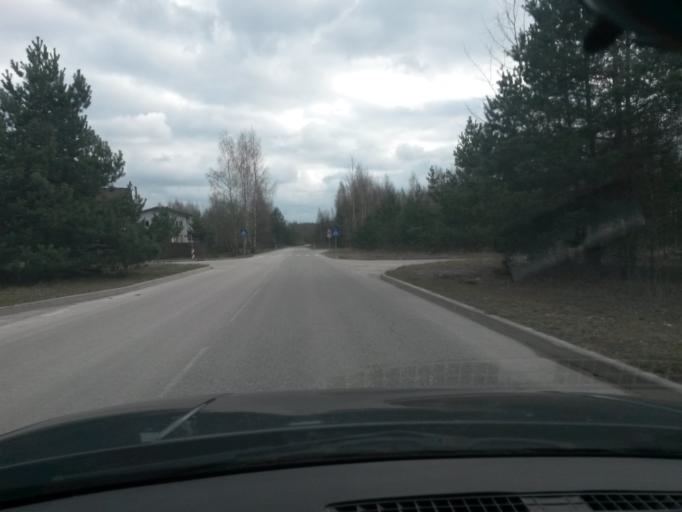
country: LV
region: Stopini
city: Ulbroka
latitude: 56.8989
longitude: 24.2472
